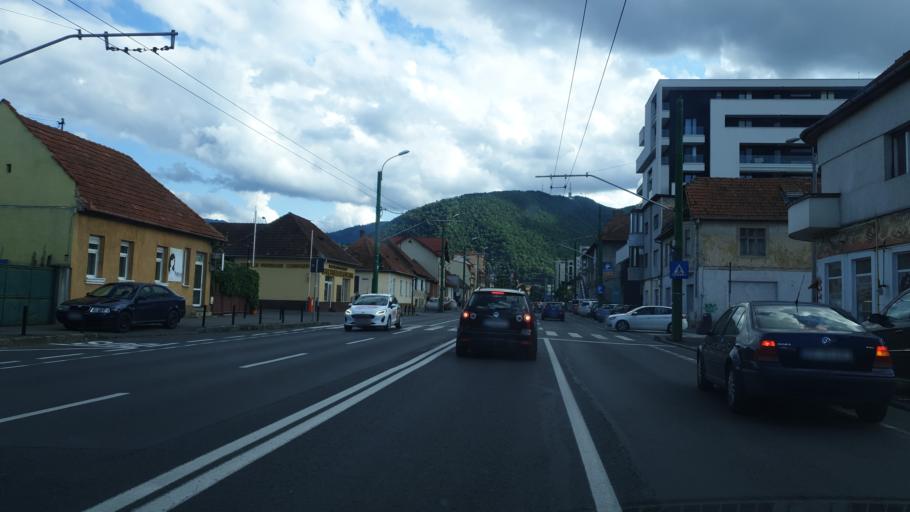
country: RO
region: Brasov
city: Brasov
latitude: 45.6569
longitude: 25.6061
